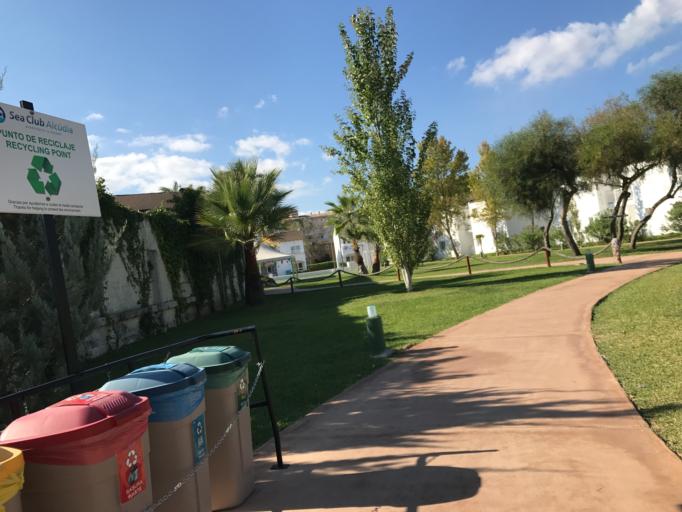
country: ES
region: Balearic Islands
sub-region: Illes Balears
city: Alcudia
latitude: 39.8358
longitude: 3.1129
